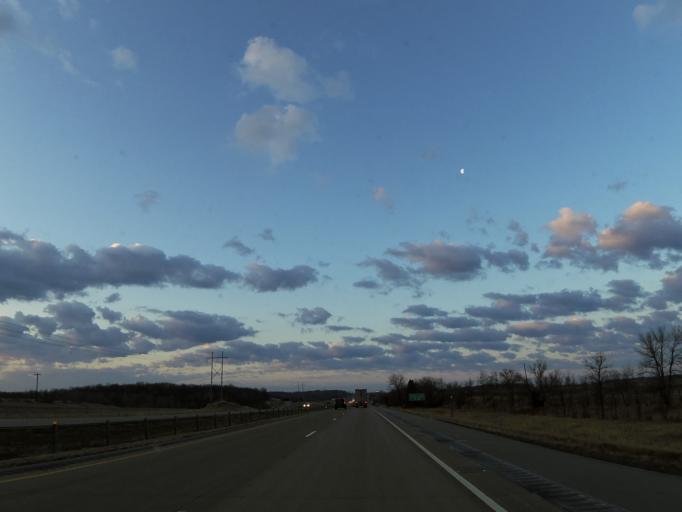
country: US
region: Minnesota
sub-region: Scott County
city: Elko New Market
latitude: 44.4892
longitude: -93.2920
